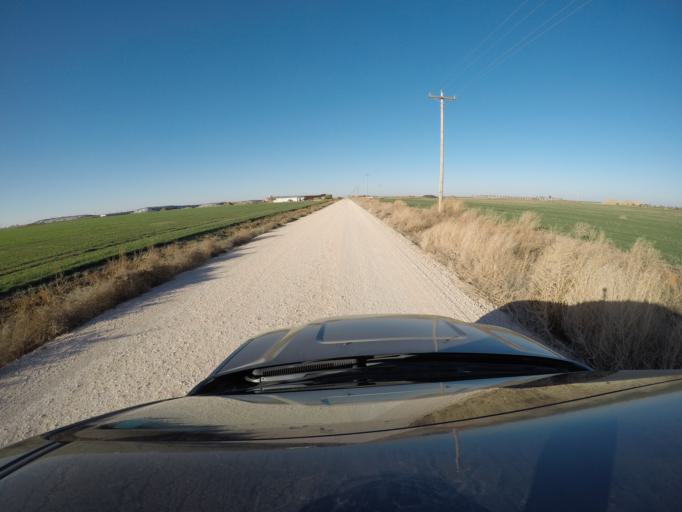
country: US
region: New Mexico
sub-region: Curry County
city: Texico
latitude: 34.3664
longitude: -103.1083
